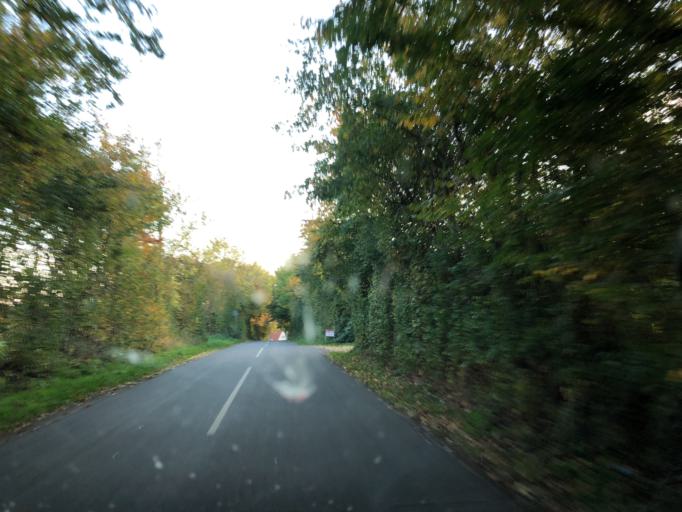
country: DK
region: South Denmark
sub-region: Vejle Kommune
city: Borkop
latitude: 55.6110
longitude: 9.6489
